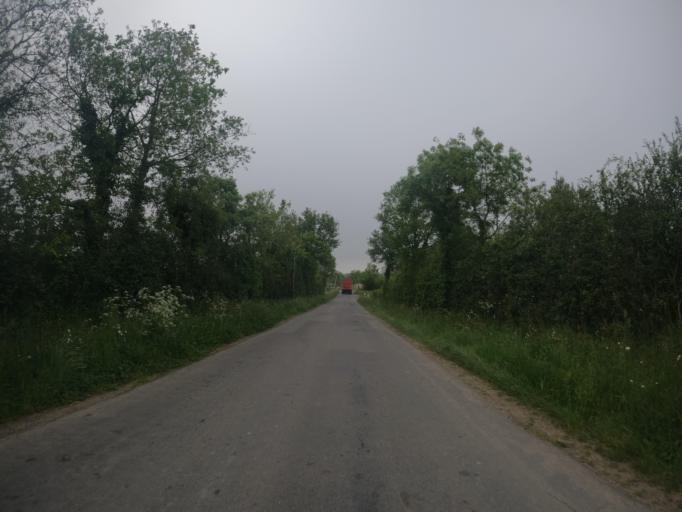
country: FR
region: Poitou-Charentes
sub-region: Departement des Deux-Sevres
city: Chiche
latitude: 46.8961
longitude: -0.3405
